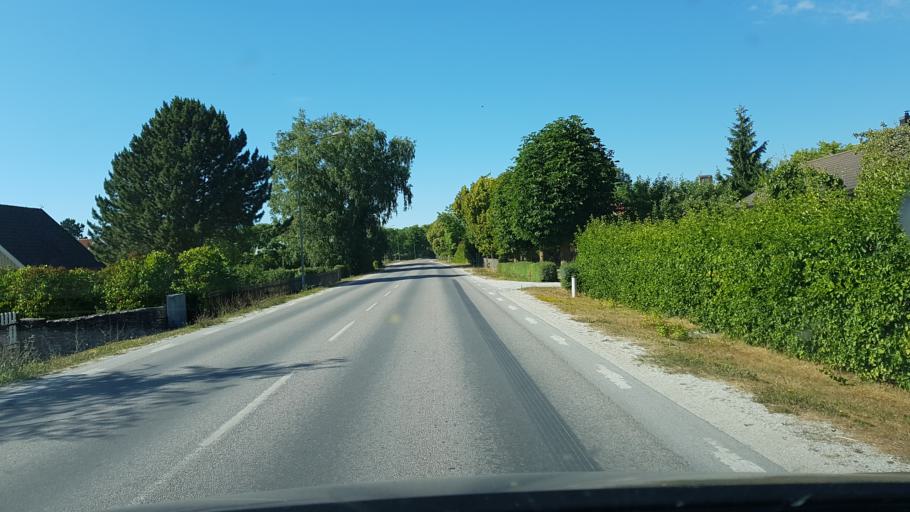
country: SE
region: Gotland
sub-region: Gotland
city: Klintehamn
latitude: 57.4354
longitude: 18.1458
